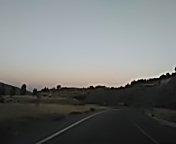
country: ES
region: Castille and Leon
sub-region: Provincia de Salamanca
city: Vallejera de Riofrio
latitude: 40.3995
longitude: -5.7370
